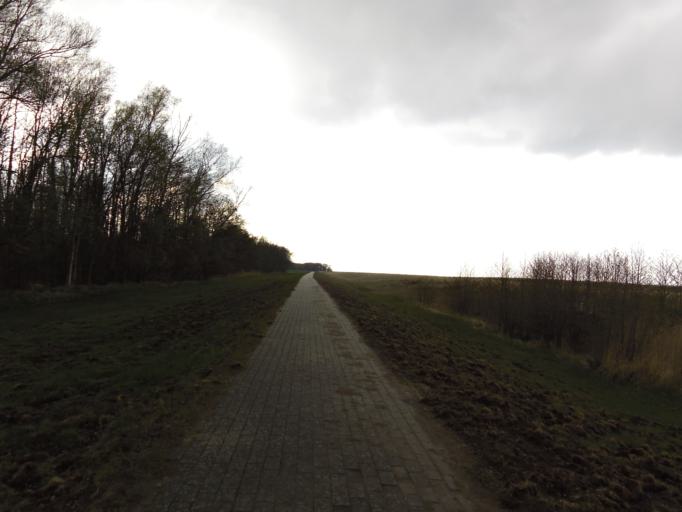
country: DE
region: Mecklenburg-Vorpommern
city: Zingst
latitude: 54.4399
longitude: 12.7787
